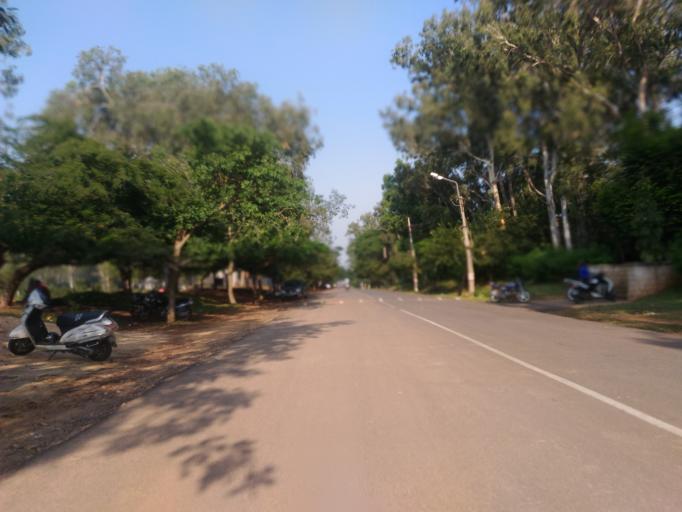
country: IN
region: Karnataka
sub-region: Bangalore Urban
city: Bangalore
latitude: 12.9383
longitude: 77.5002
